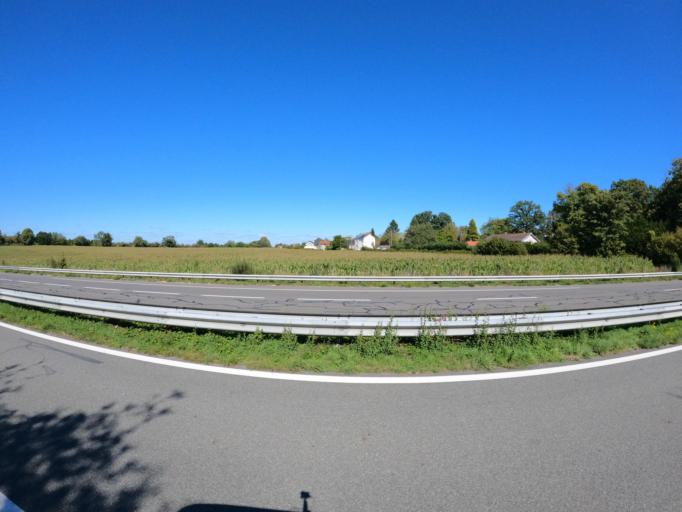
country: FR
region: Limousin
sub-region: Departement de la Creuse
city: La Souterraine
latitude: 46.2241
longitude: 1.4830
